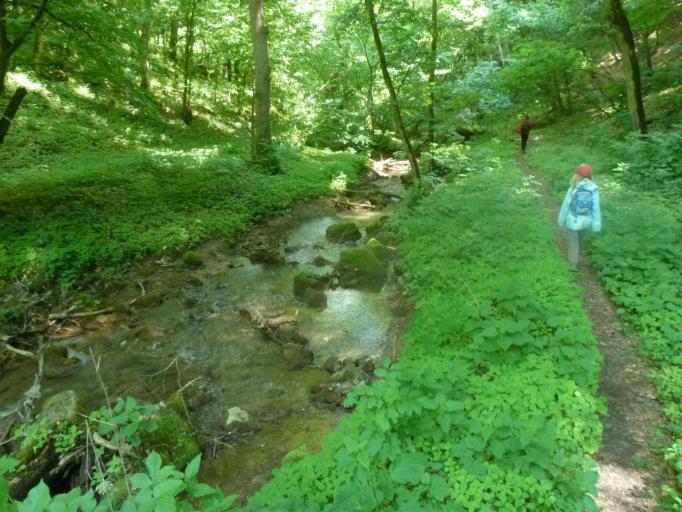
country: HU
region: Borsod-Abauj-Zemplen
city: Rudabanya
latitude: 48.4893
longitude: 20.5281
